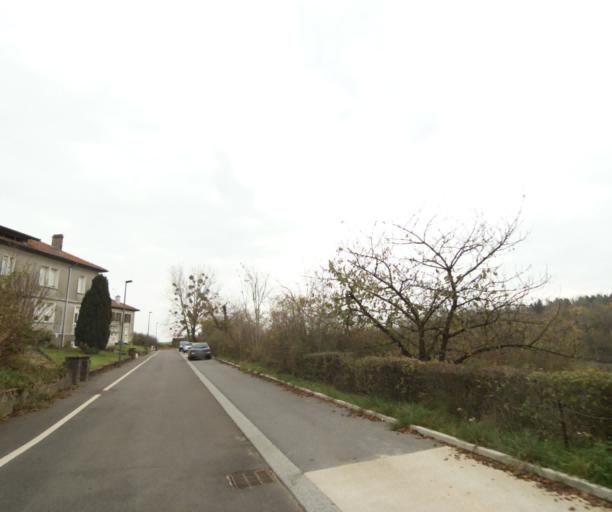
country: FR
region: Lorraine
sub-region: Departement de Meurthe-et-Moselle
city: Mancieulles
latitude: 49.2891
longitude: 5.9034
